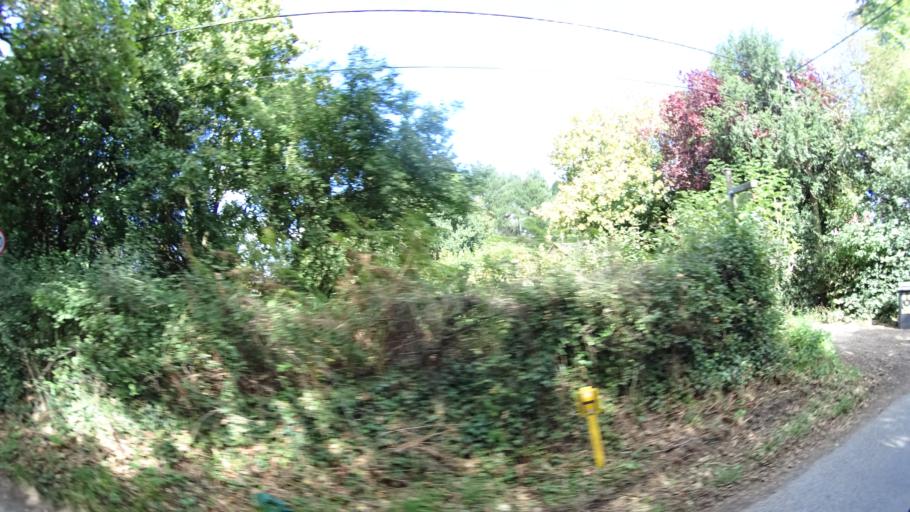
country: GB
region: England
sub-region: Hampshire
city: Romsey
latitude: 51.0089
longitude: -1.5208
